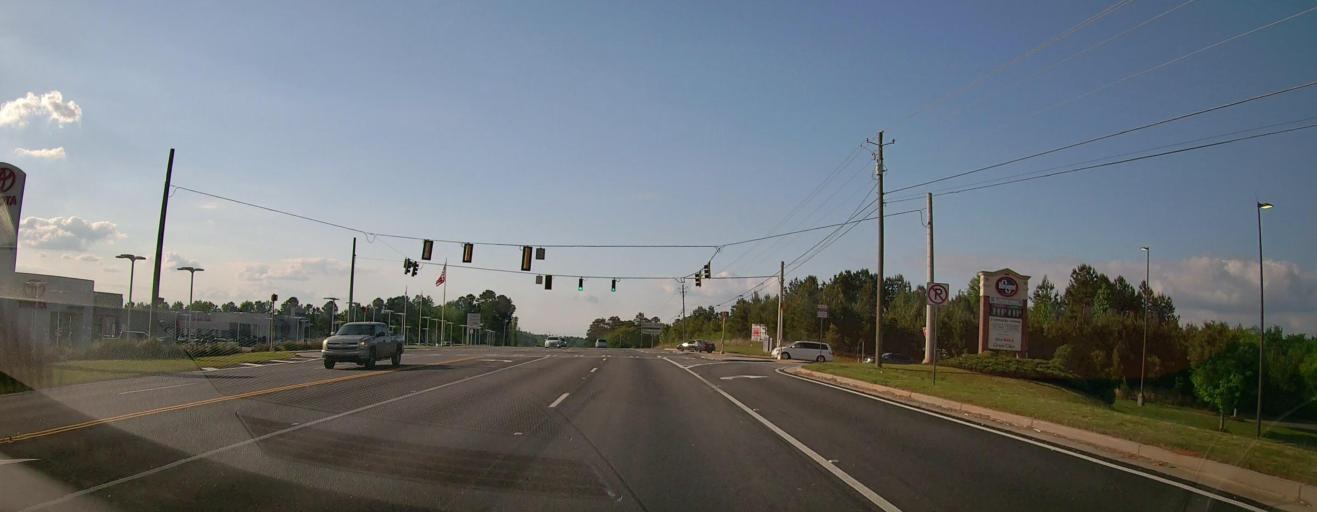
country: US
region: Georgia
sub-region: Baldwin County
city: Milledgeville
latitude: 33.1529
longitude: -83.2744
